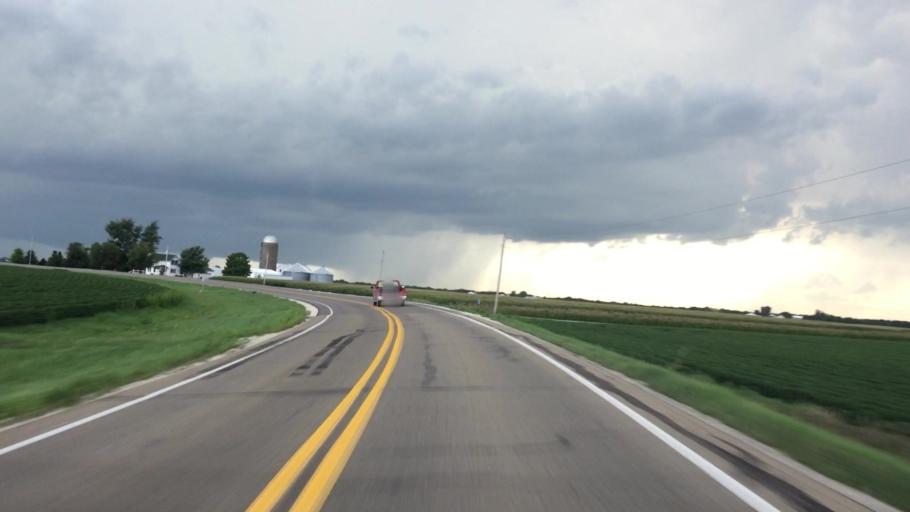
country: US
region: Iowa
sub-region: Henry County
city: New London
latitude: 40.7822
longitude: -91.4781
